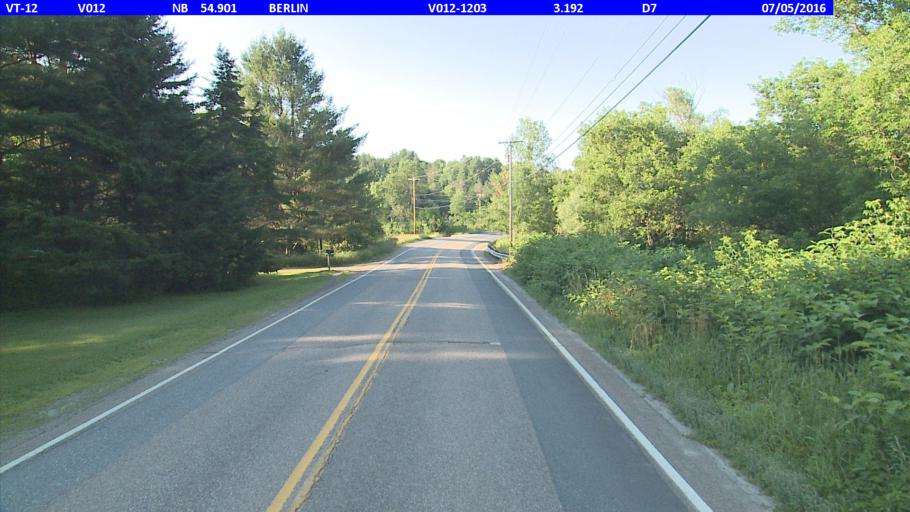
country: US
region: Vermont
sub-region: Washington County
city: Northfield
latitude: 44.2134
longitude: -72.6286
